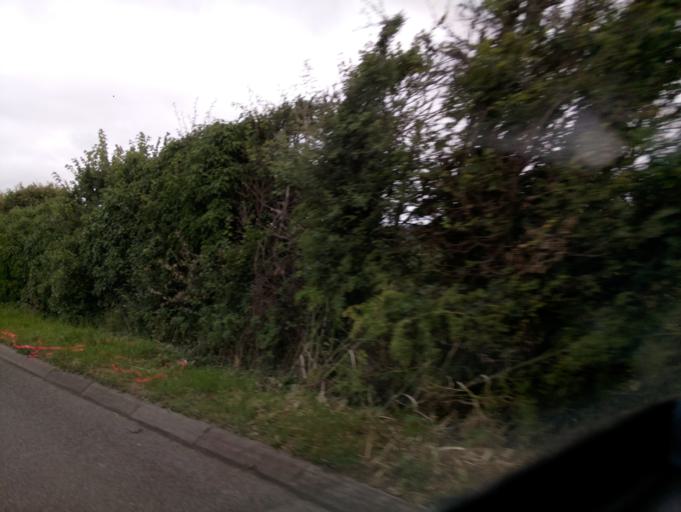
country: GB
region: England
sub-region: Gloucestershire
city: Uckington
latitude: 51.9478
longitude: -2.1600
